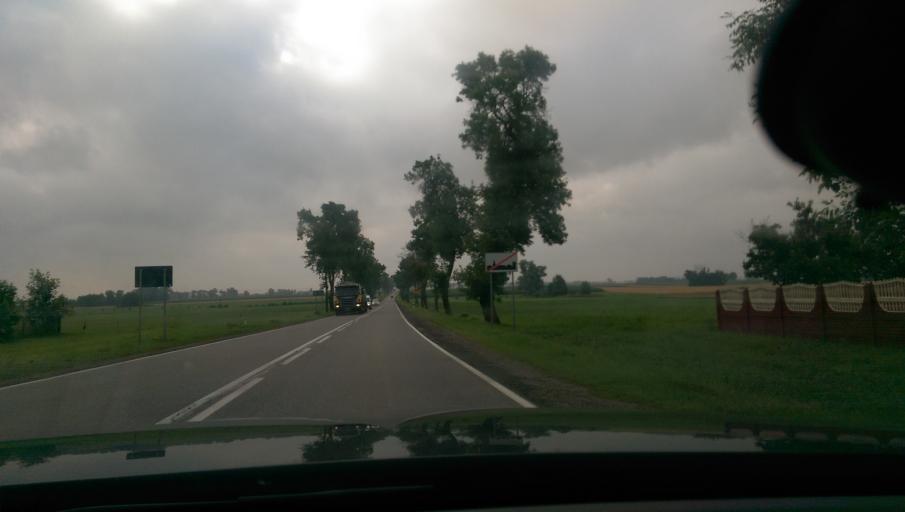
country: PL
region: Masovian Voivodeship
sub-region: Powiat przasnyski
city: Przasnysz
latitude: 53.0666
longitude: 20.8628
